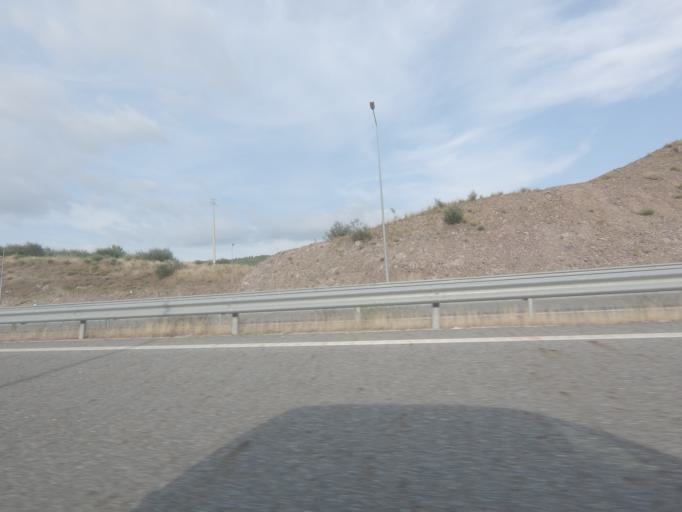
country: PT
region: Vila Real
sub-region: Boticas
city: Boticas
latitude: 41.6494
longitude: -7.5817
